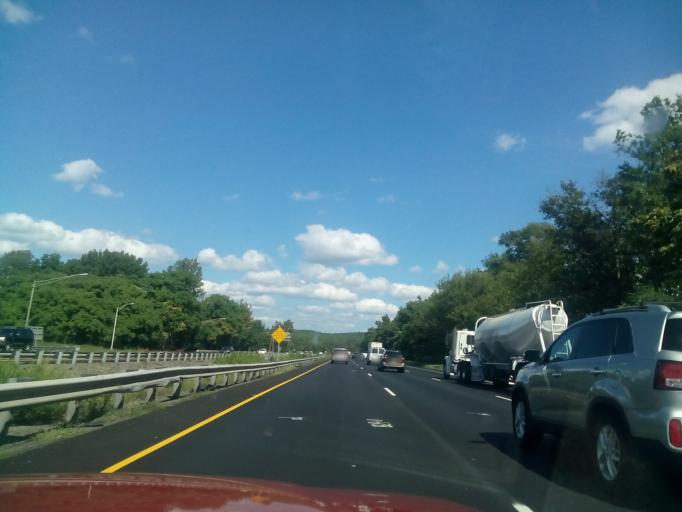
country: US
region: New Jersey
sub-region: Morris County
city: Wharton
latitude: 40.9086
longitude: -74.5749
